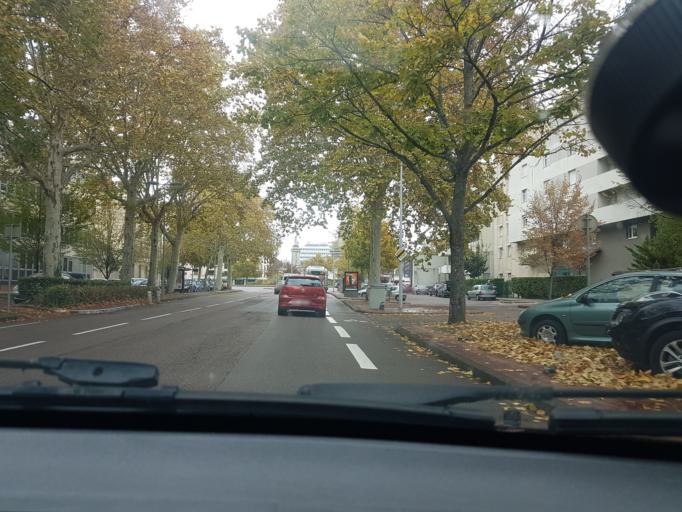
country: FR
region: Bourgogne
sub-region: Departement de la Cote-d'Or
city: Saint-Apollinaire
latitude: 47.3203
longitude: 5.0520
